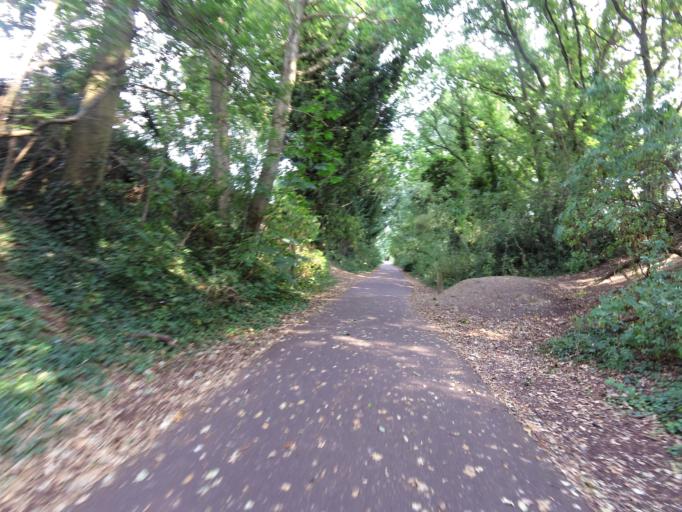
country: GB
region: England
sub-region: Hertfordshire
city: St Albans
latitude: 51.7501
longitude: -0.3049
